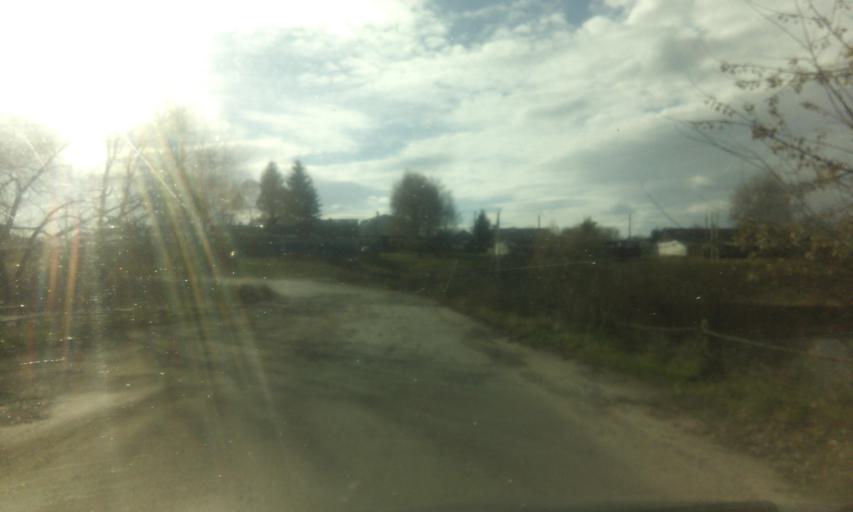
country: RU
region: Tula
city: Dubovka
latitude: 53.9477
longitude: 38.0282
